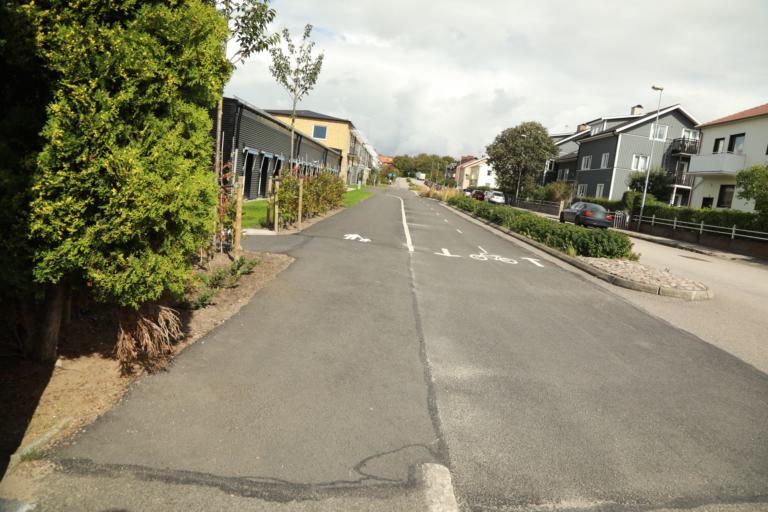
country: SE
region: Halland
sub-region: Varbergs Kommun
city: Varberg
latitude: 57.1131
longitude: 12.2569
